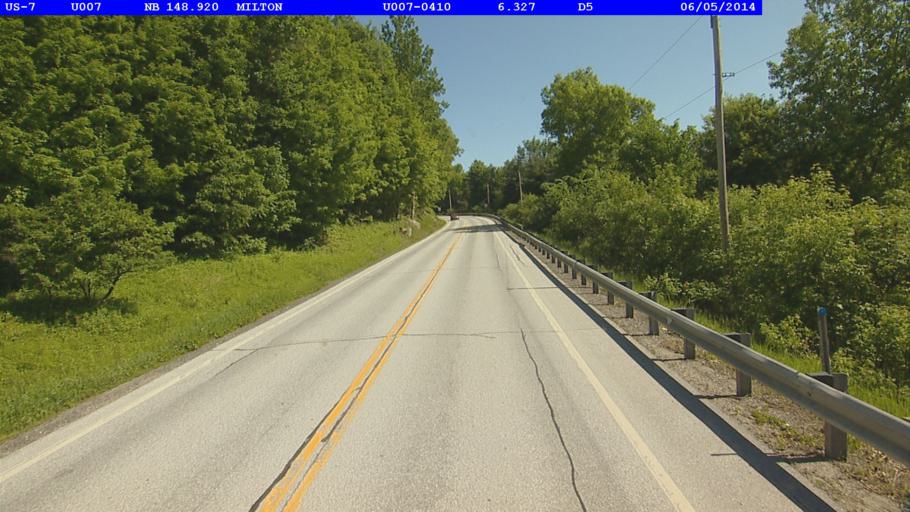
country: US
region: Vermont
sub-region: Chittenden County
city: Milton
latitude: 44.6578
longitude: -73.1129
